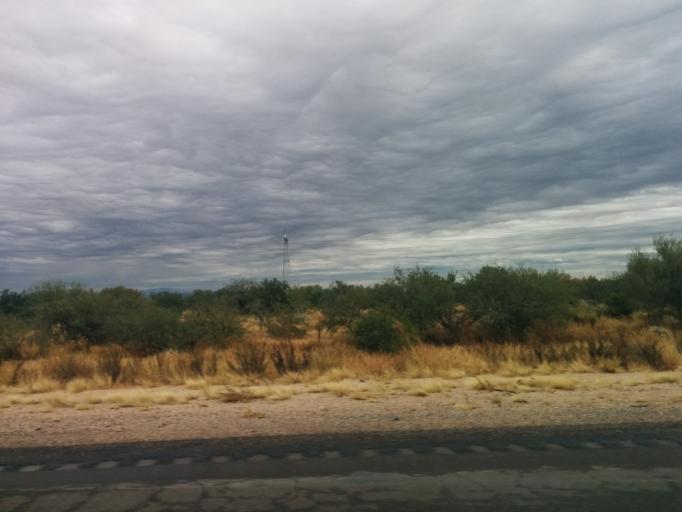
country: MX
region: Sonora
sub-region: San Miguel de Horcasitas
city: Las Mercedes [Agropecuaria]
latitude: 29.5371
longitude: -111.0099
